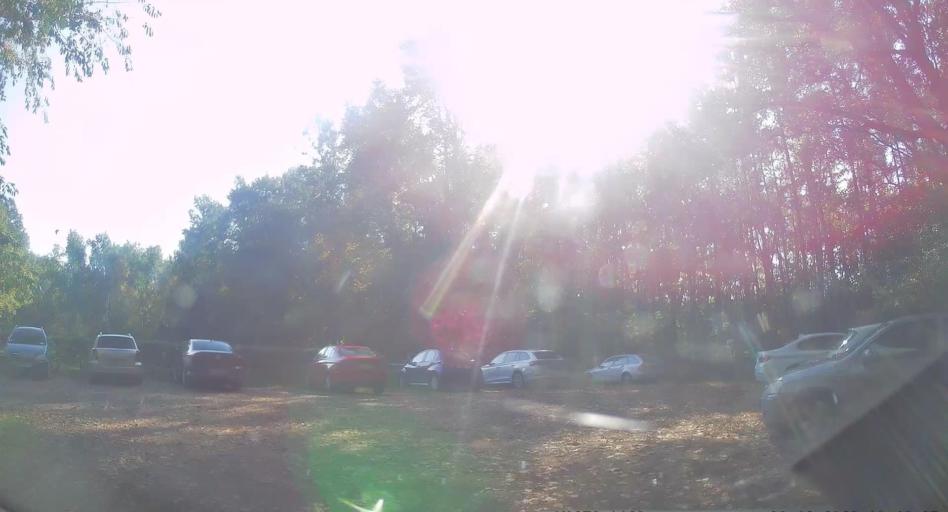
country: PL
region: Lesser Poland Voivodeship
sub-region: Powiat wielicki
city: Niepolomice
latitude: 50.0146
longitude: 20.2402
